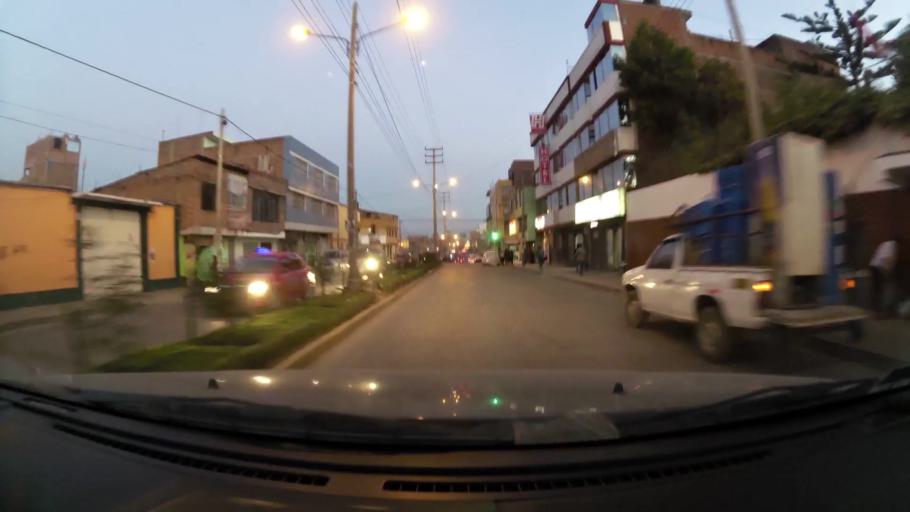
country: PE
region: Junin
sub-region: Provincia de Huancayo
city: El Tambo
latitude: -12.0585
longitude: -75.2220
